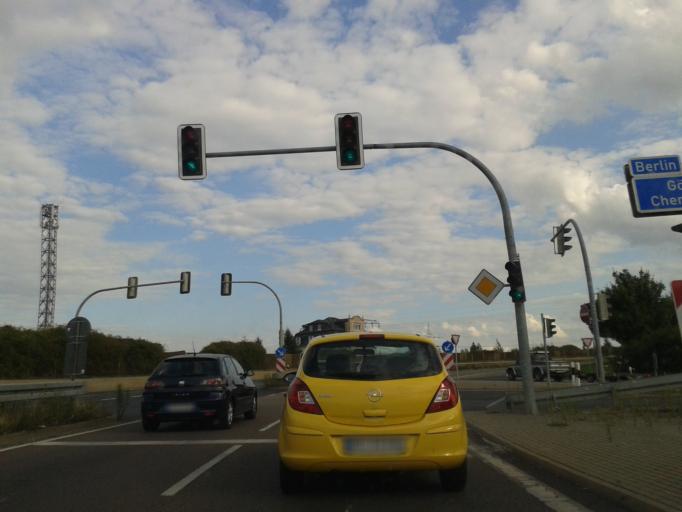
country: DE
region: Saxony
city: Bannewitz
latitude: 51.0101
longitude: 13.7295
